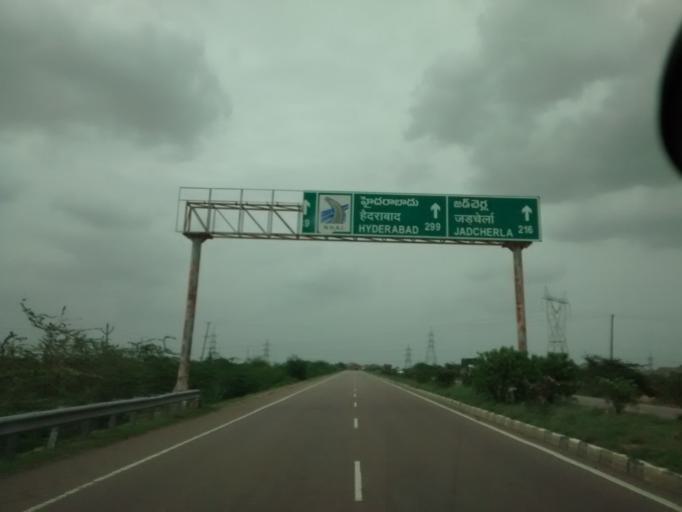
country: IN
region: Andhra Pradesh
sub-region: Kurnool
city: Ramapuram
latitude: 15.1432
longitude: 77.6641
